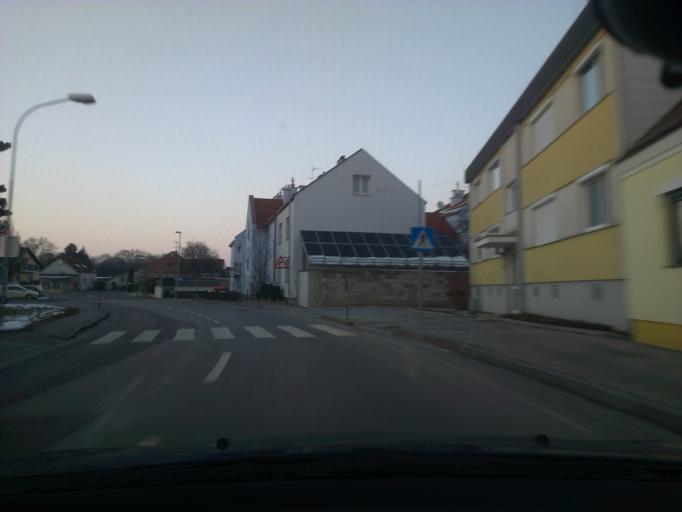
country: AT
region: Lower Austria
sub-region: Politischer Bezirk Bruck an der Leitha
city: Enzersdorf an der Fischa
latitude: 48.0877
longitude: 16.6091
